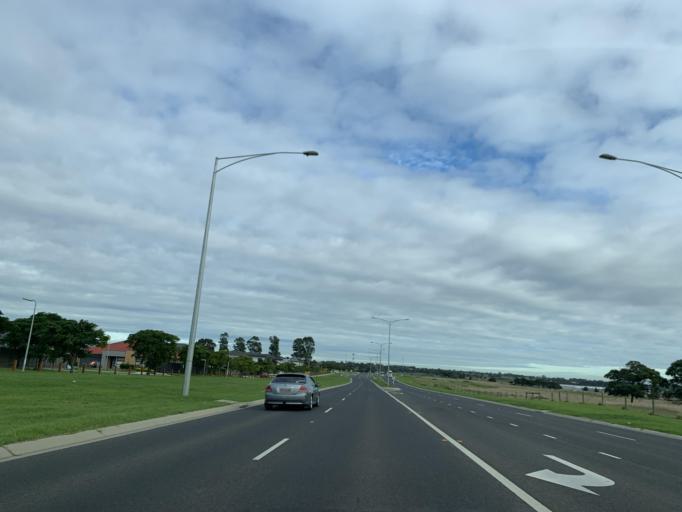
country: AU
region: Victoria
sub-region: Frankston
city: Skye
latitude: -38.1080
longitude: 145.2417
